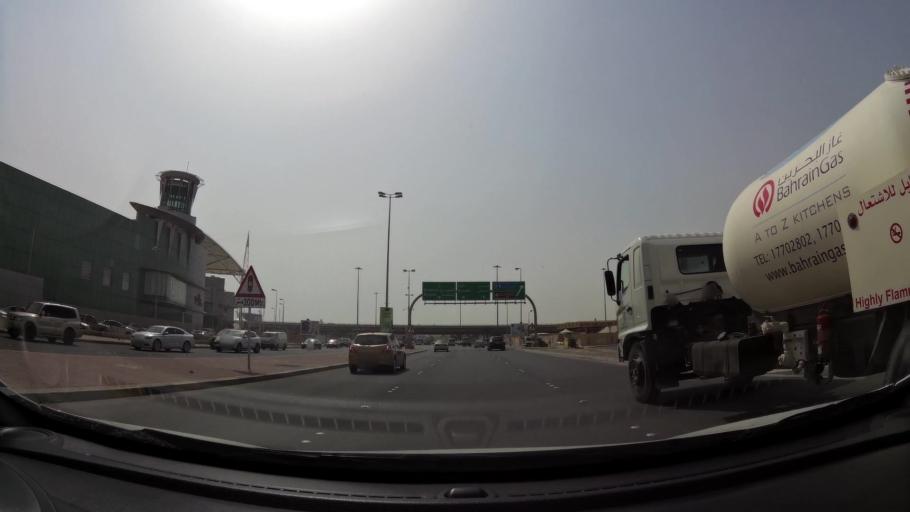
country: BH
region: Manama
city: Jidd Hafs
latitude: 26.2329
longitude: 50.5338
